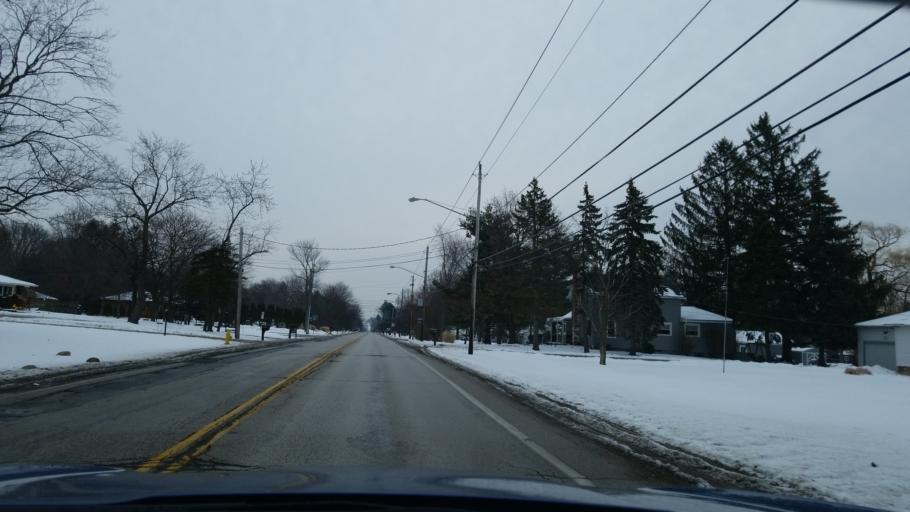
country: US
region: Ohio
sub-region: Cuyahoga County
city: North Royalton
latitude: 41.3138
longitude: -81.7115
